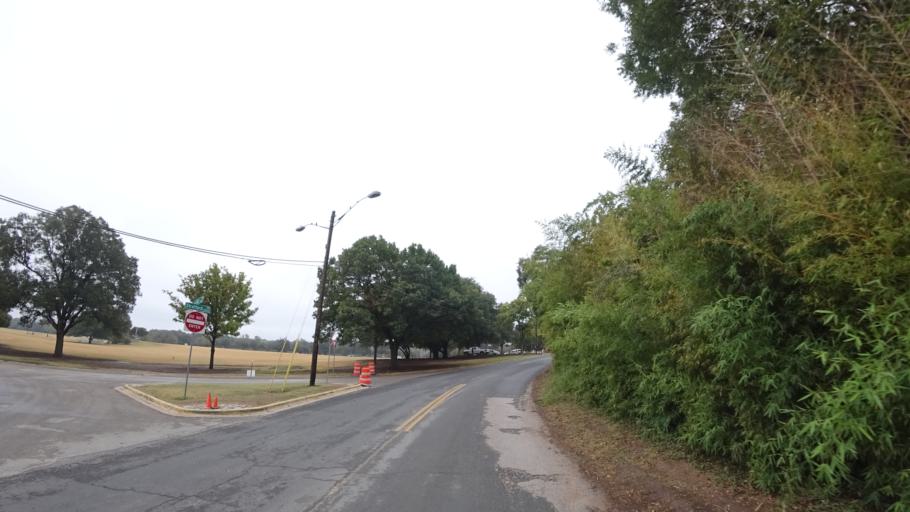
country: US
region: Texas
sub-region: Travis County
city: Rollingwood
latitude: 30.2692
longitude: -97.7705
